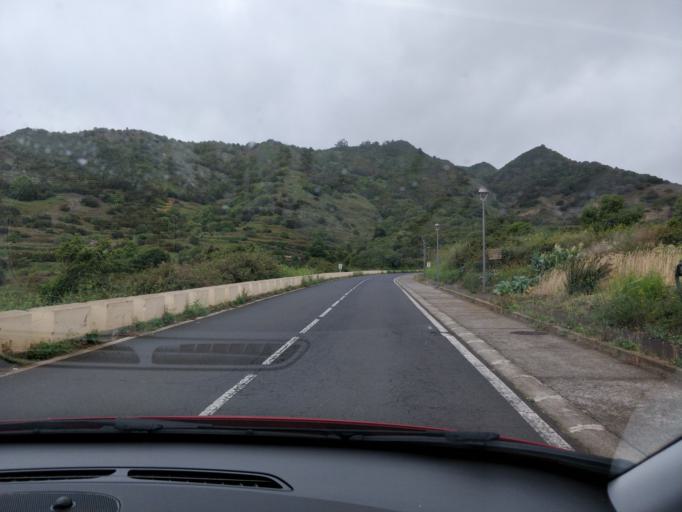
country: ES
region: Canary Islands
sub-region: Provincia de Santa Cruz de Tenerife
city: Tanque
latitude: 28.3290
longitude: -16.8443
